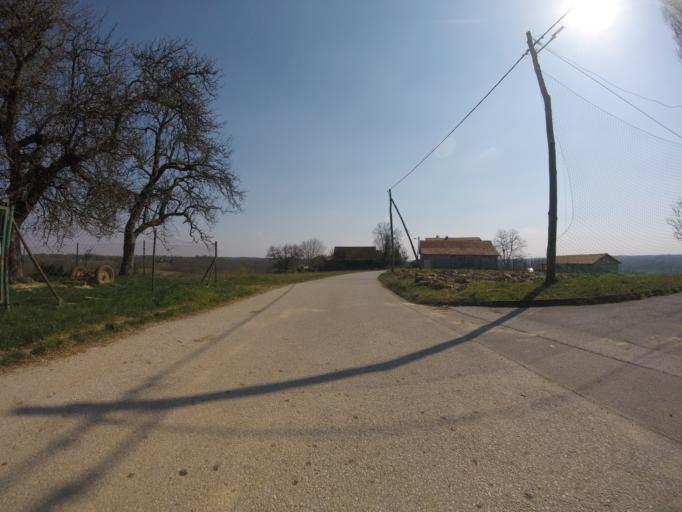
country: HR
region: Sisacko-Moslavacka
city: Gvozd
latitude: 45.5187
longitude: 15.9243
